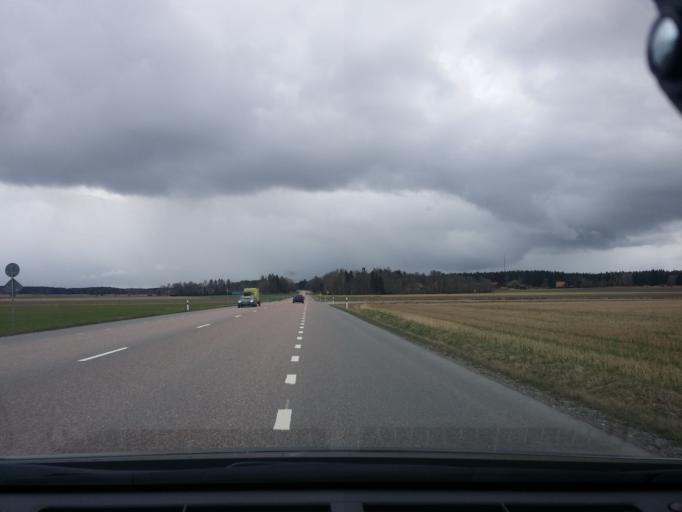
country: SE
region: Uppsala
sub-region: Enkopings Kommun
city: Irsta
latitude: 59.7458
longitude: 16.9486
